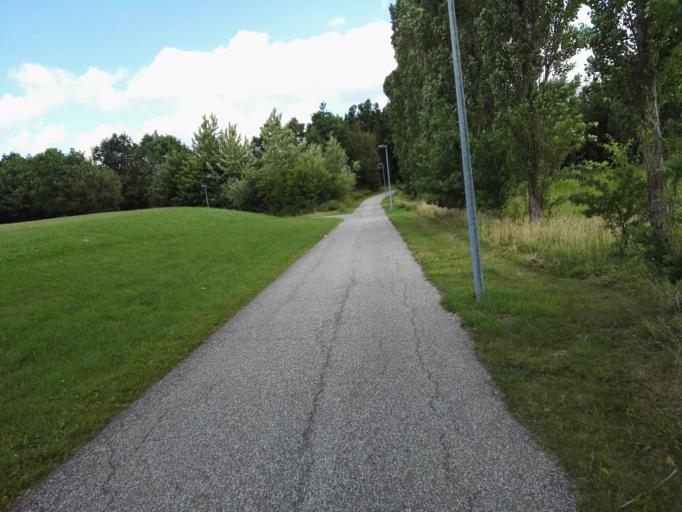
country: DK
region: Capital Region
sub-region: Ballerup Kommune
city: Ballerup
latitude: 55.7337
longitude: 12.3929
